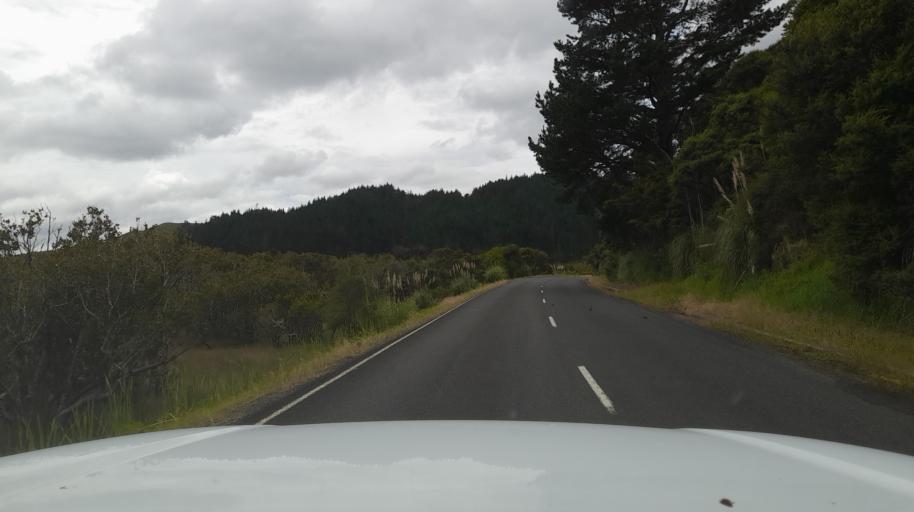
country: NZ
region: Northland
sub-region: Far North District
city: Kaitaia
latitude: -35.3640
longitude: 173.4336
